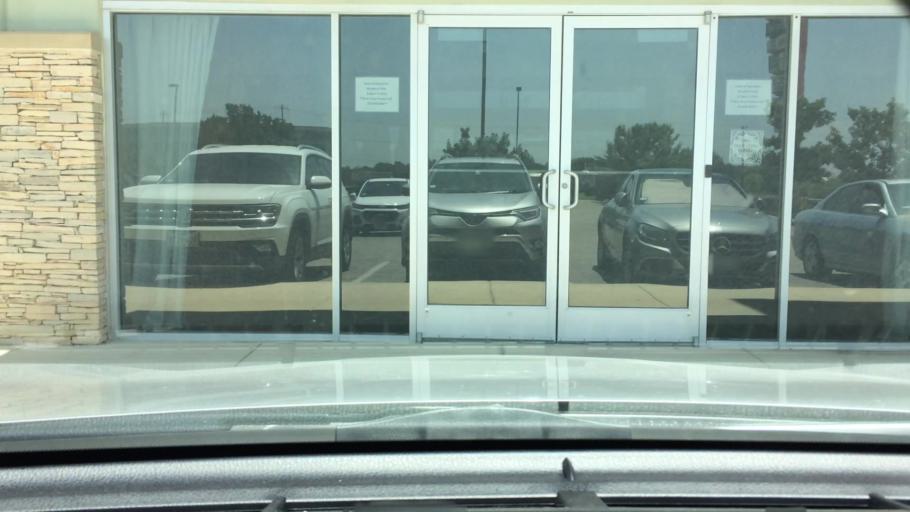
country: US
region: Texas
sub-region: Bexar County
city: Shavano Park
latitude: 29.5959
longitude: -98.5745
